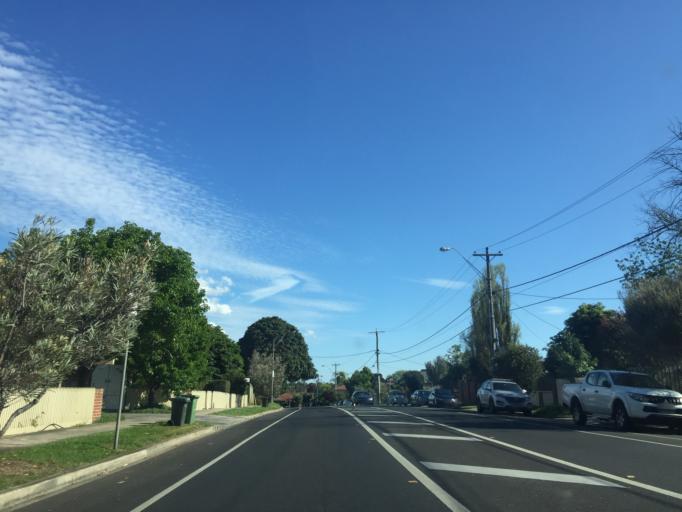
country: AU
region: Victoria
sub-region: Banyule
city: Bellfield
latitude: -37.7651
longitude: 145.0355
